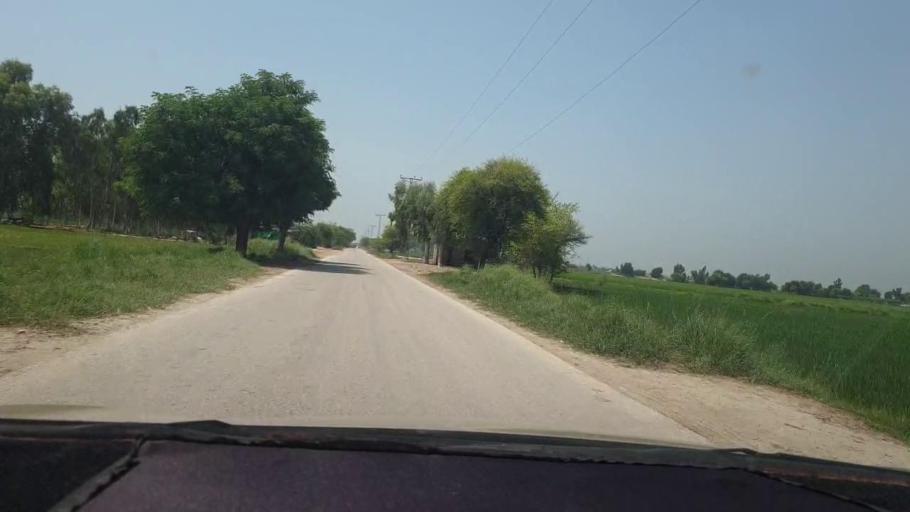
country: PK
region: Sindh
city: Kambar
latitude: 27.5988
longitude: 68.0251
